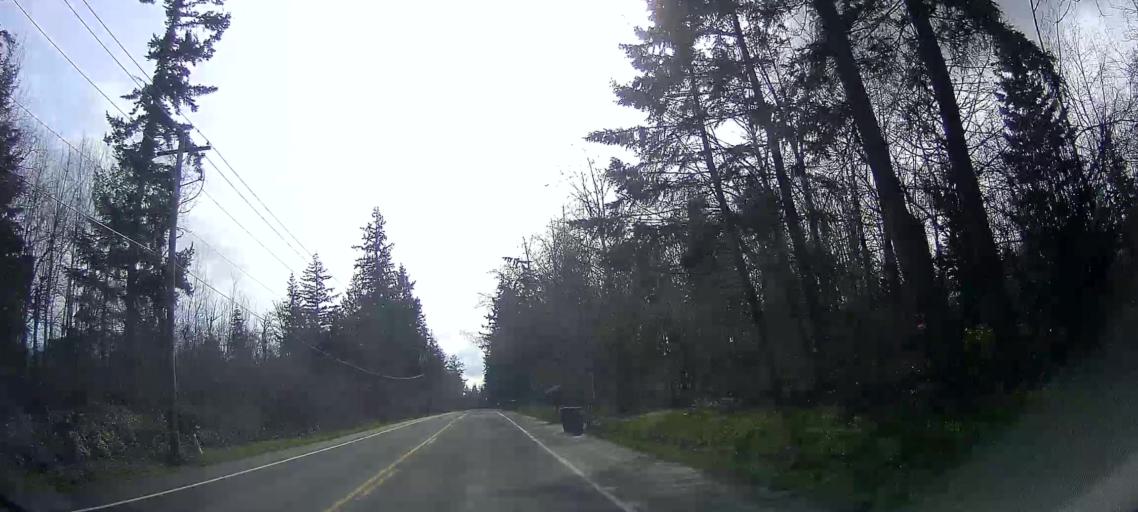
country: US
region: Washington
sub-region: Island County
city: Camano
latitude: 48.1572
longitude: -122.4753
